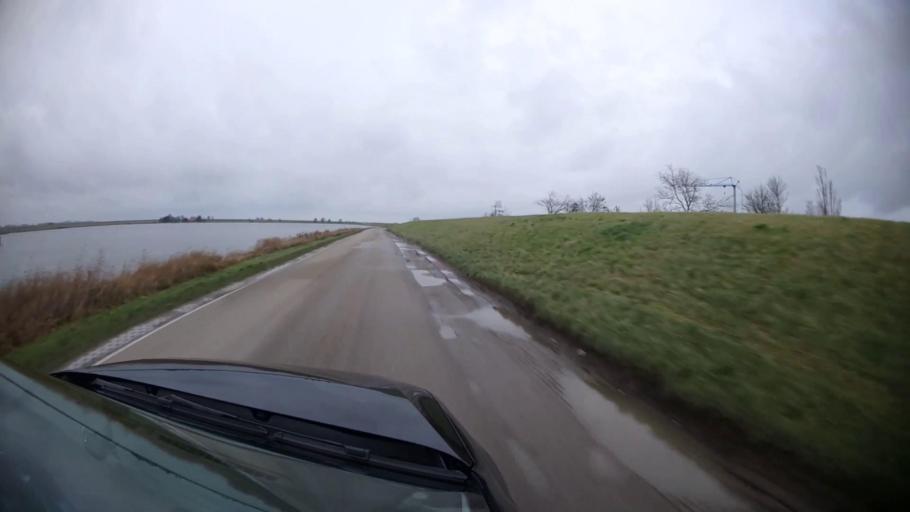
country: NL
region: North Holland
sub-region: Gemeente Waterland
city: Marken
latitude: 52.4305
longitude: 5.0723
